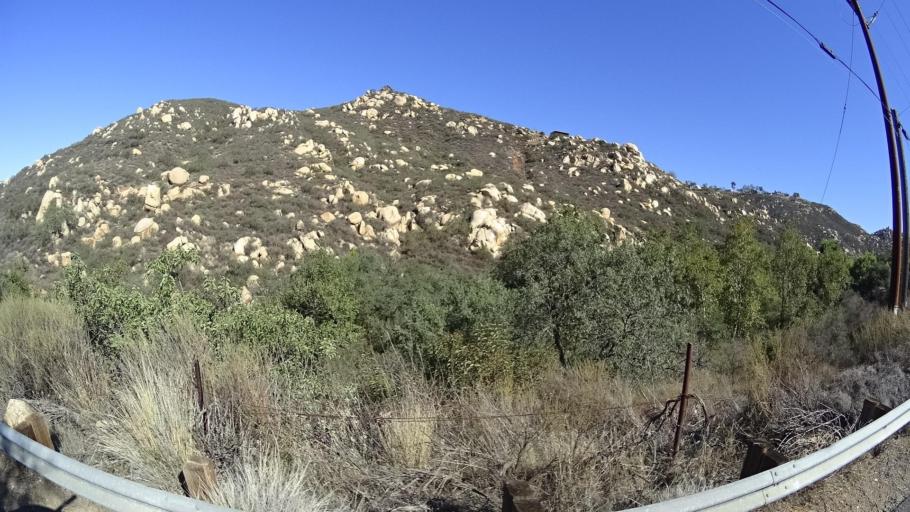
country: US
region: California
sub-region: San Diego County
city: Jamul
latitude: 32.7091
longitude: -116.7867
